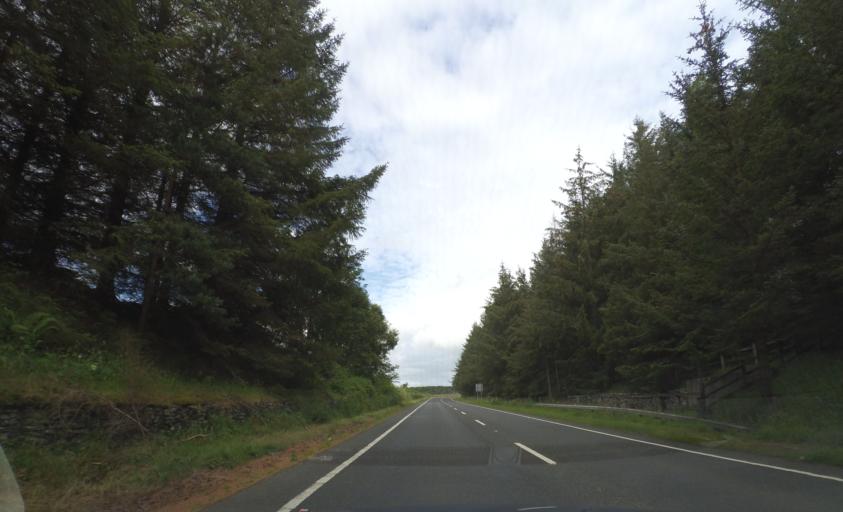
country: GB
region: Scotland
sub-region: The Scottish Borders
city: Selkirk
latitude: 55.5054
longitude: -2.8391
